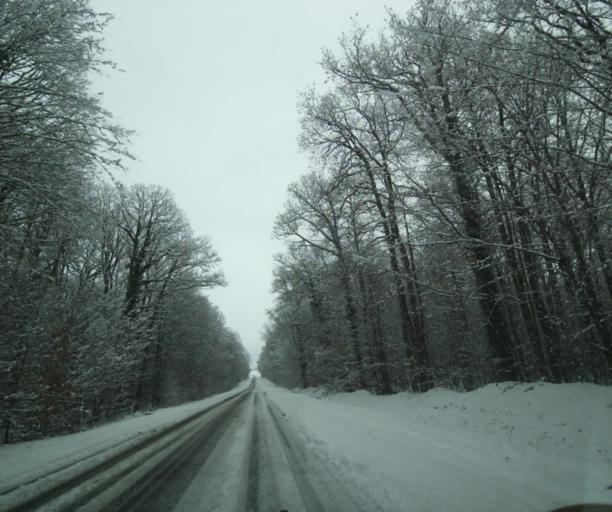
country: FR
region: Champagne-Ardenne
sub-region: Departement de la Haute-Marne
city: Montier-en-Der
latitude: 48.5274
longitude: 4.7948
